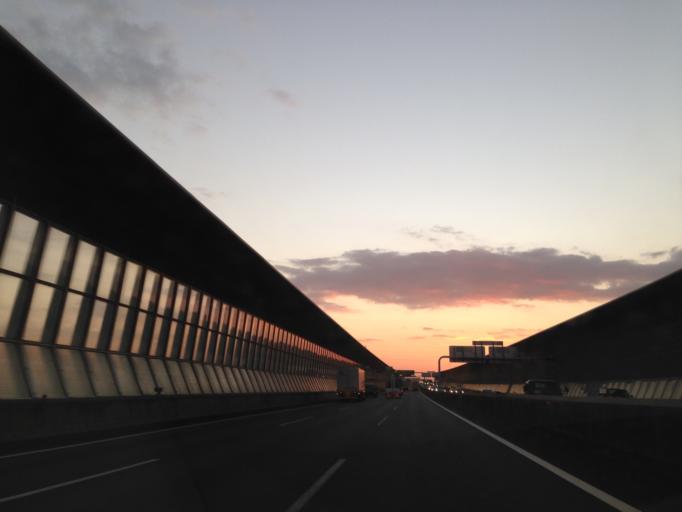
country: JP
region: Aichi
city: Obu
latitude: 35.0480
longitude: 136.9144
